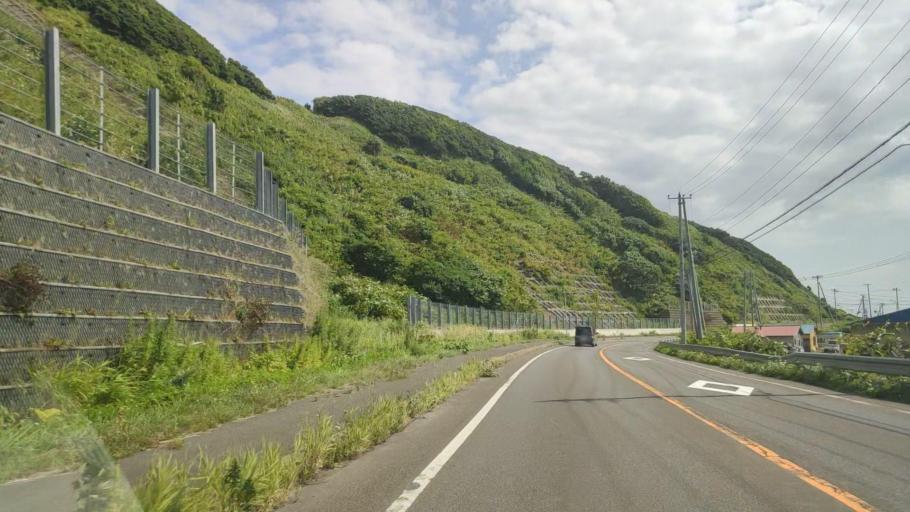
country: JP
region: Hokkaido
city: Rumoi
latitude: 44.2254
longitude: 141.6555
